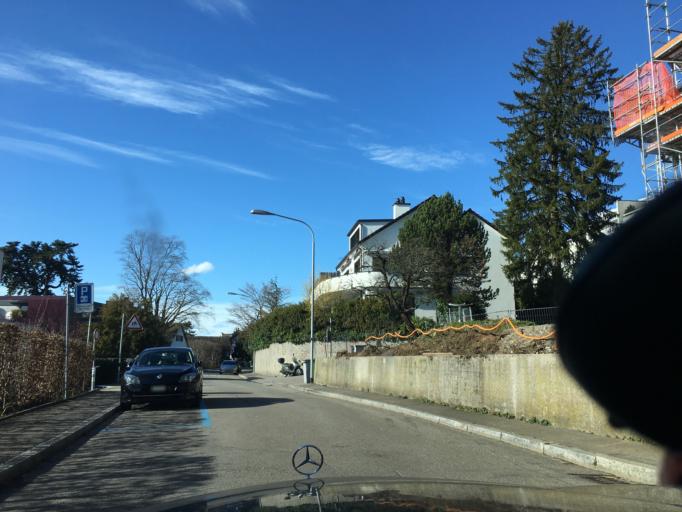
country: CH
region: Zurich
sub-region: Bezirk Zuerich
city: Zuerich (Kreis 8) / Weinegg
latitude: 47.3565
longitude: 8.5791
